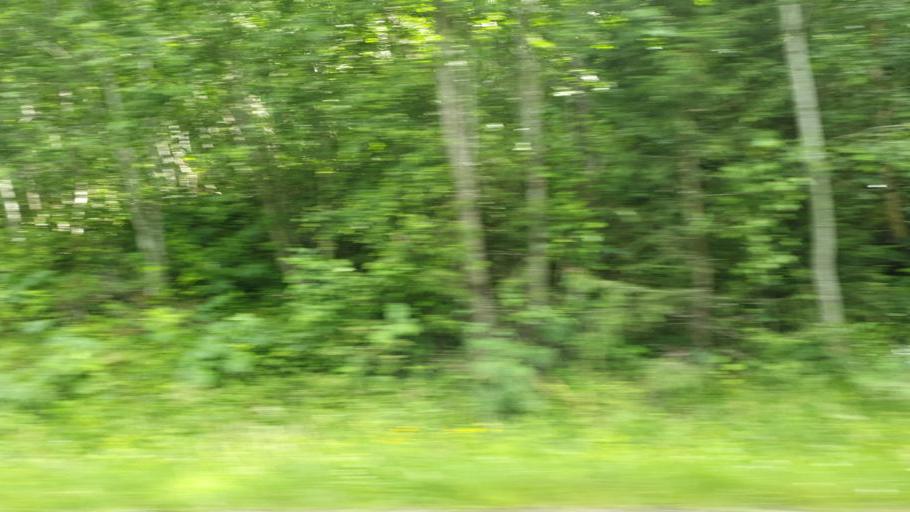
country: NO
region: Oppland
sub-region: Dovre
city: Dovre
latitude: 61.8451
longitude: 9.3454
